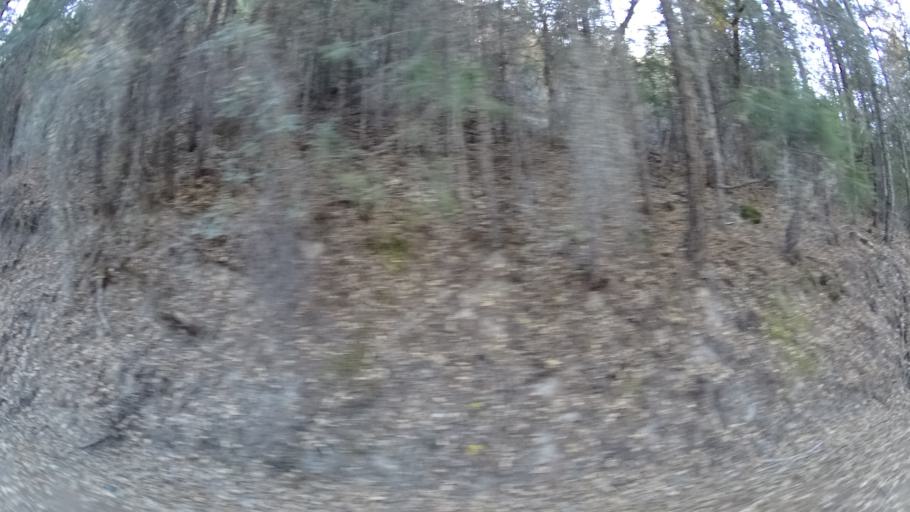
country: US
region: California
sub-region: Siskiyou County
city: Yreka
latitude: 41.8305
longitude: -122.9553
